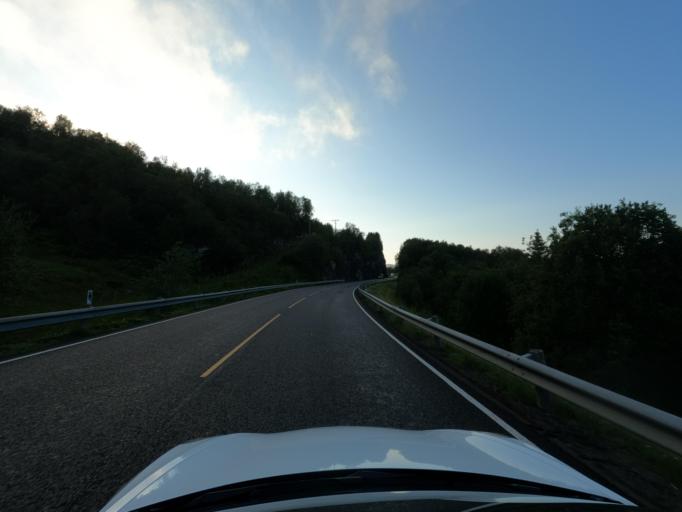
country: NO
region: Troms
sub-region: Skanland
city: Evenskjer
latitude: 68.6716
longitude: 16.5709
